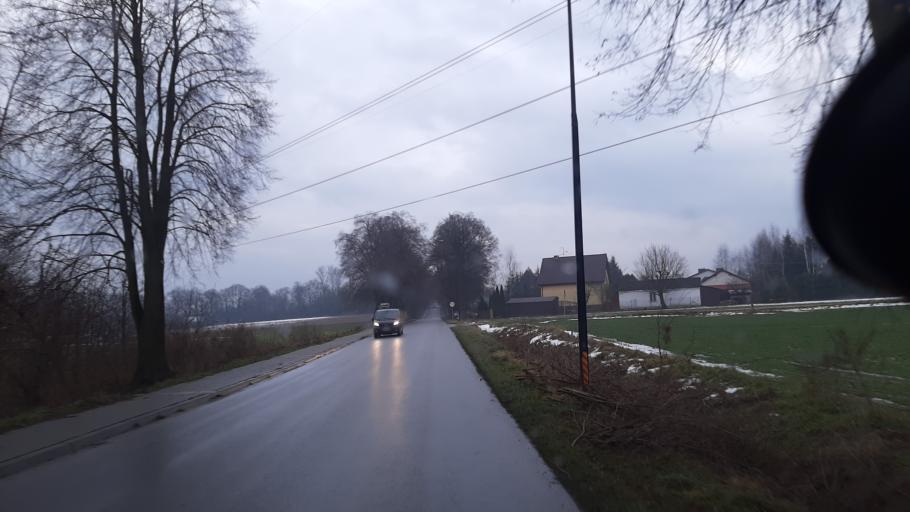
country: PL
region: Lublin Voivodeship
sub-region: Powiat lubelski
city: Lublin
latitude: 51.3312
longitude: 22.5555
